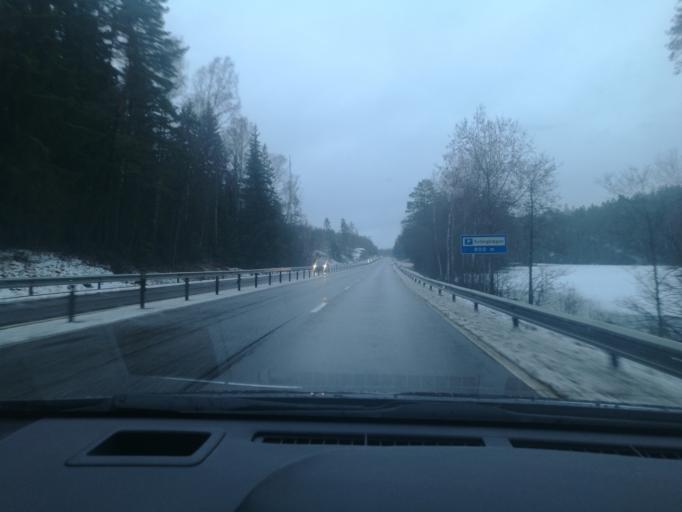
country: SE
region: OEstergoetland
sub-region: Norrkopings Kommun
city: Jursla
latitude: 58.7426
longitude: 16.1732
